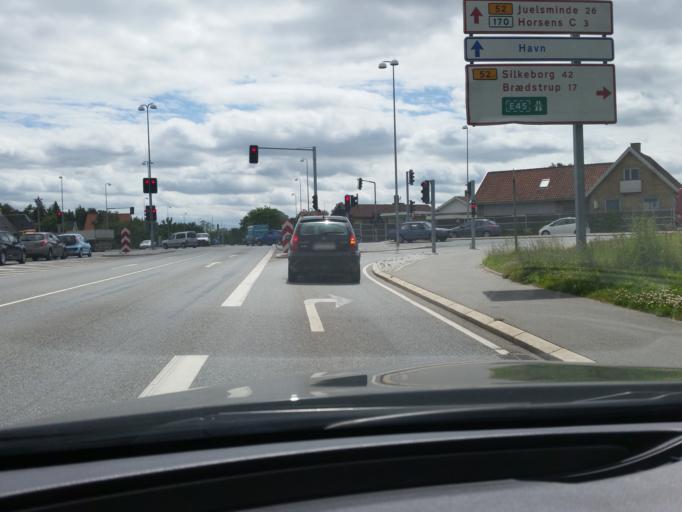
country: DK
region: Central Jutland
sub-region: Horsens Kommune
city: Horsens
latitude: 55.8750
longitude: 9.8235
